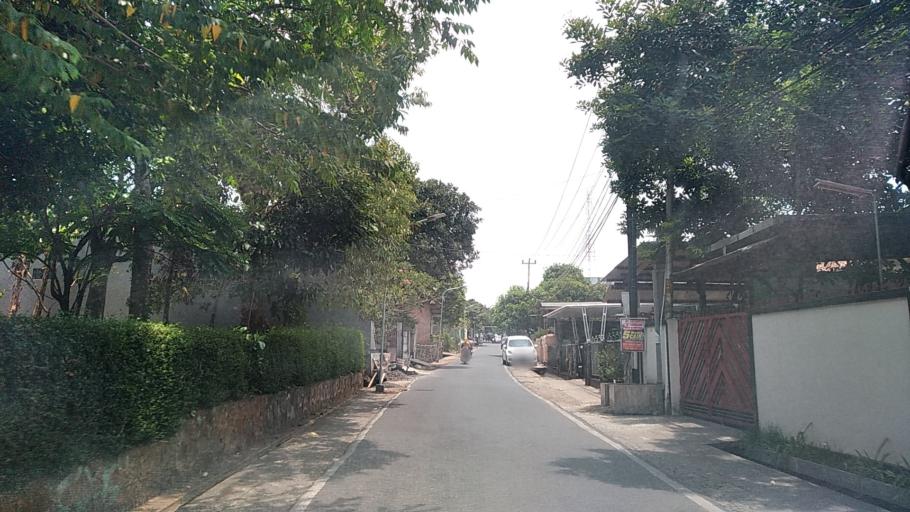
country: ID
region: Central Java
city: Semarang
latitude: -7.0611
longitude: 110.4115
